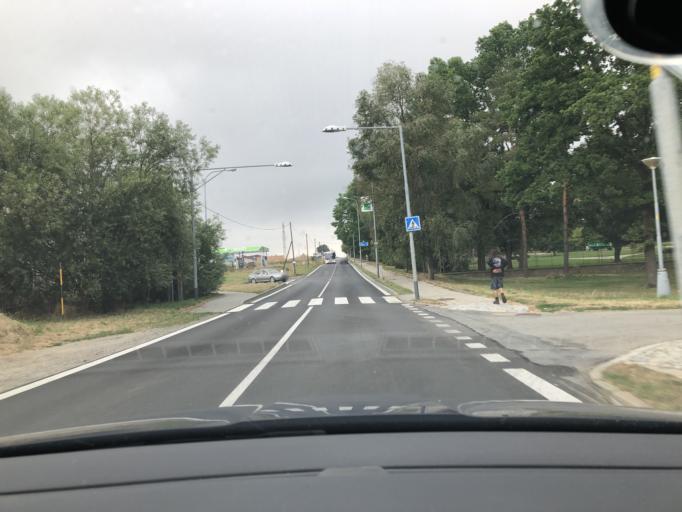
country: CZ
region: Vysocina
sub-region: Okres Trebic
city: Trebic
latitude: 49.2222
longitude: 15.8653
